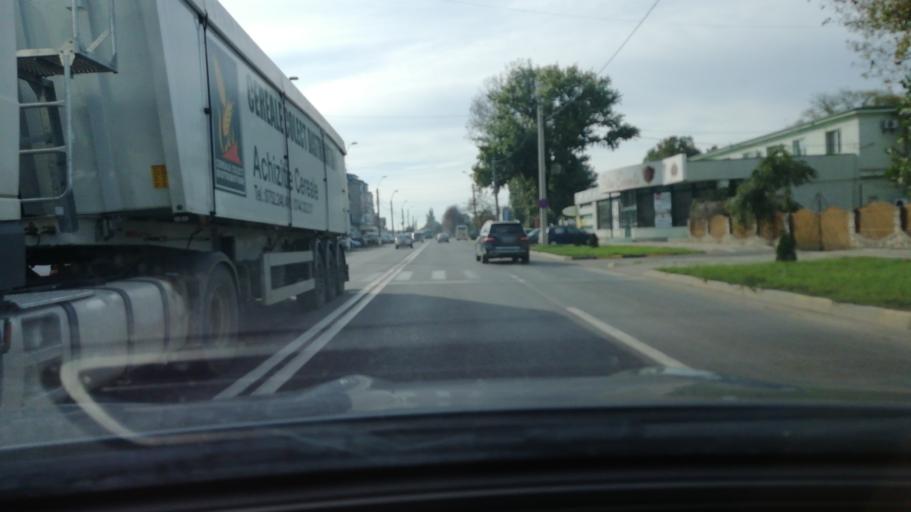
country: RO
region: Galati
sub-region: Municipiul Tecuci
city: Tecuci
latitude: 45.8294
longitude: 27.4371
